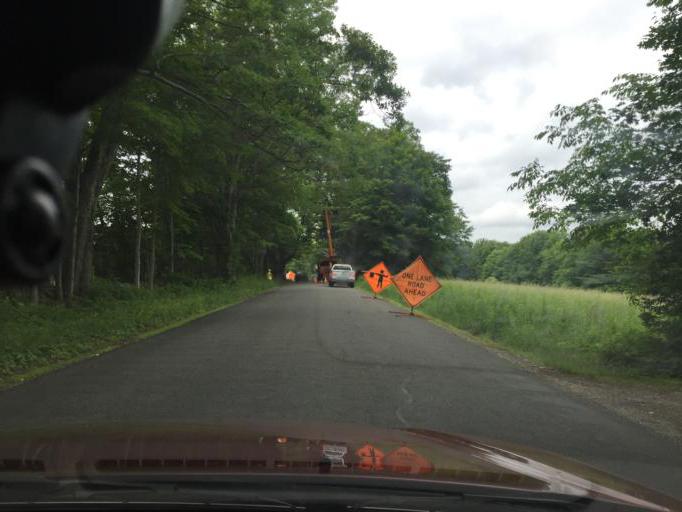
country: US
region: Connecticut
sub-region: Litchfield County
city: Litchfield
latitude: 41.7987
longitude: -73.2557
